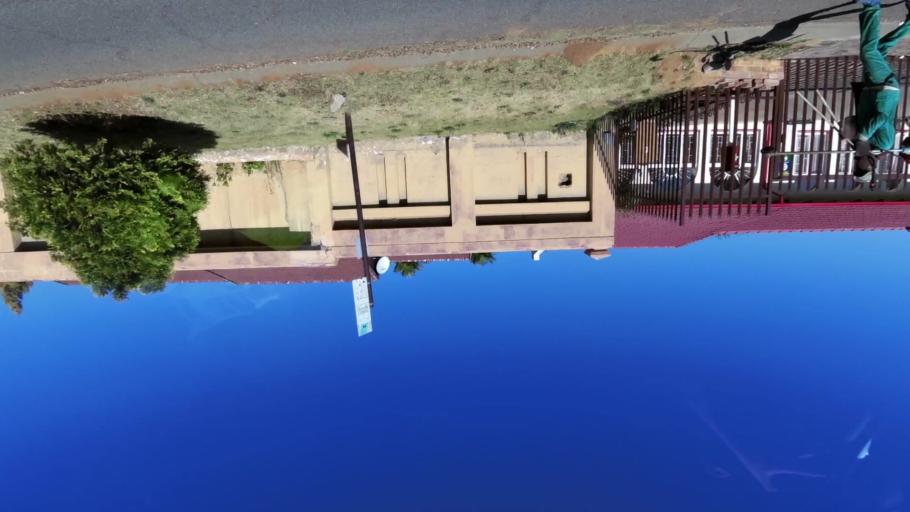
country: ZA
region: Gauteng
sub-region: City of Johannesburg Metropolitan Municipality
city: Johannesburg
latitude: -26.2480
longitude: 27.9876
